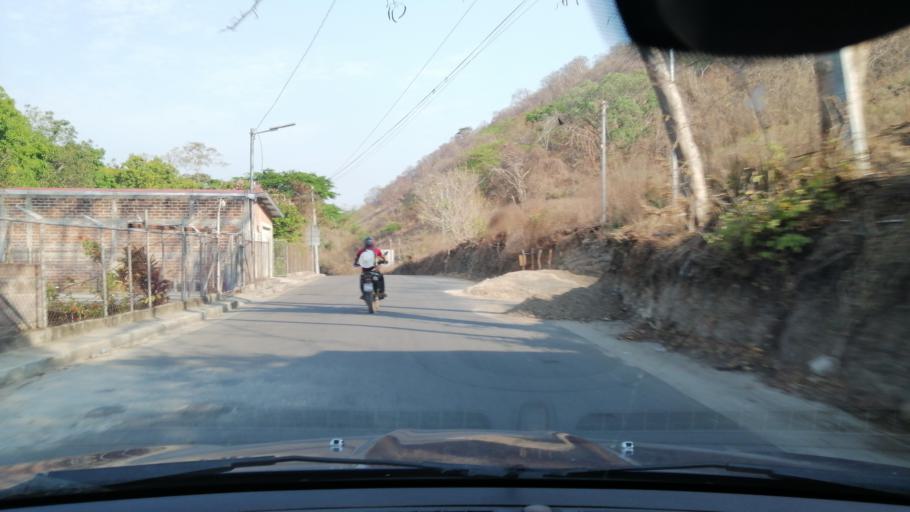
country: SV
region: Santa Ana
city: Texistepeque
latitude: 14.2240
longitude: -89.4544
